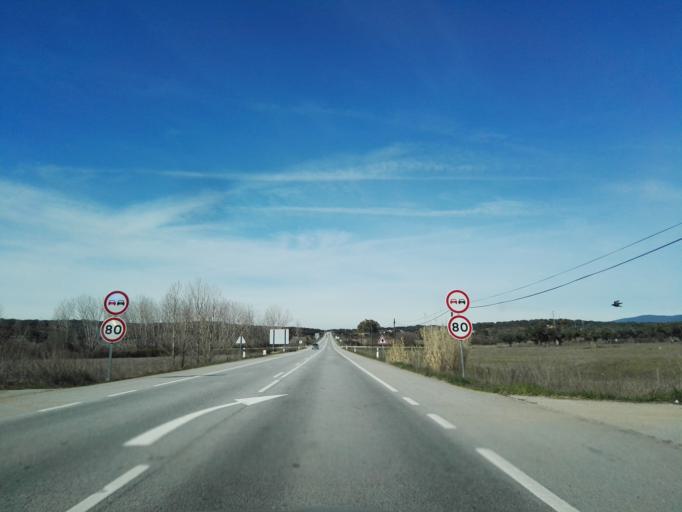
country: PT
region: Portalegre
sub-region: Arronches
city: Arronches
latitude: 39.1589
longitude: -7.3195
